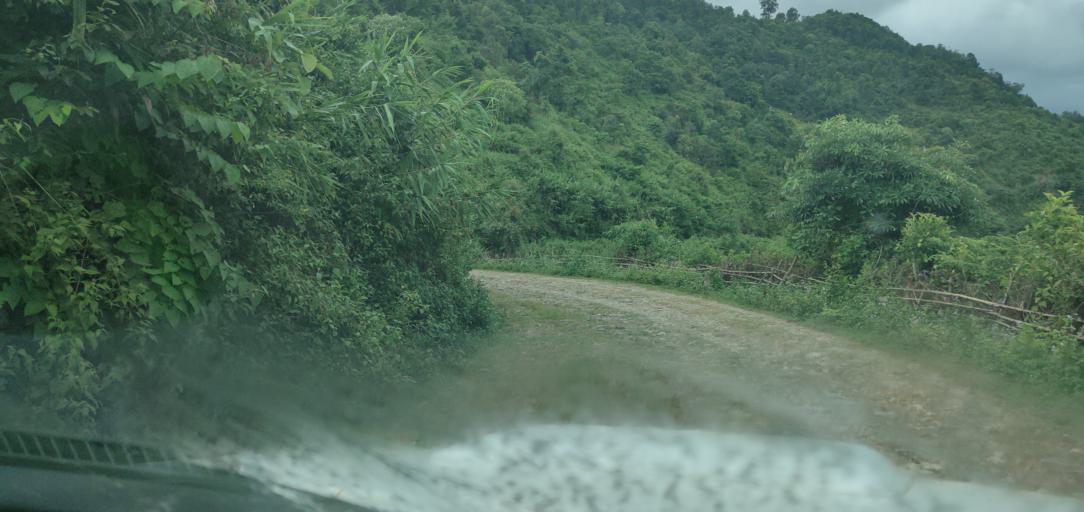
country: LA
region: Phongsali
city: Phongsali
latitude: 21.4462
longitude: 102.3051
